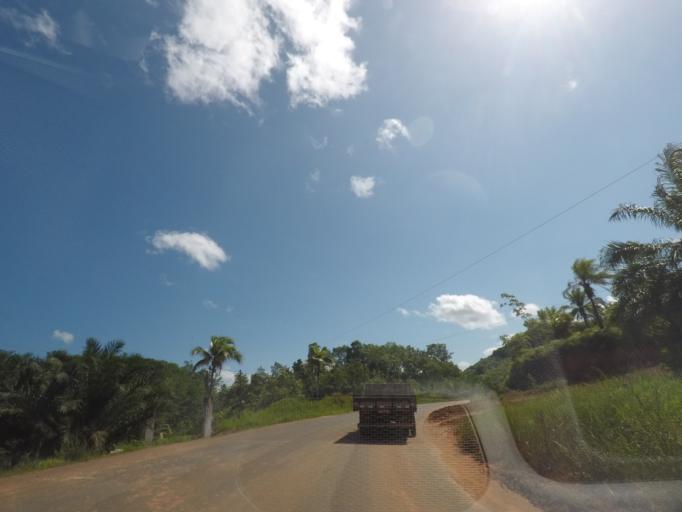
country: BR
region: Bahia
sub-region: Itubera
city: Itubera
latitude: -13.6962
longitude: -39.1330
